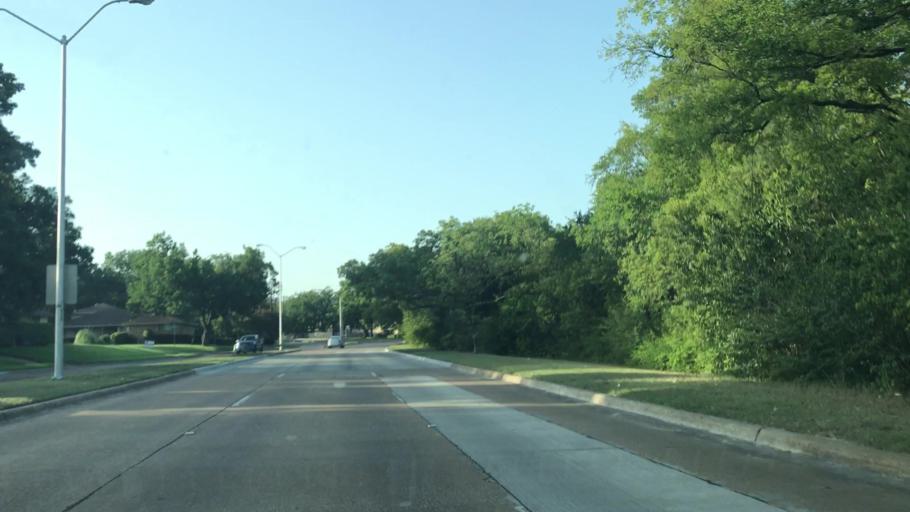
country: US
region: Texas
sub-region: Dallas County
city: Garland
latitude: 32.8501
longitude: -96.7029
